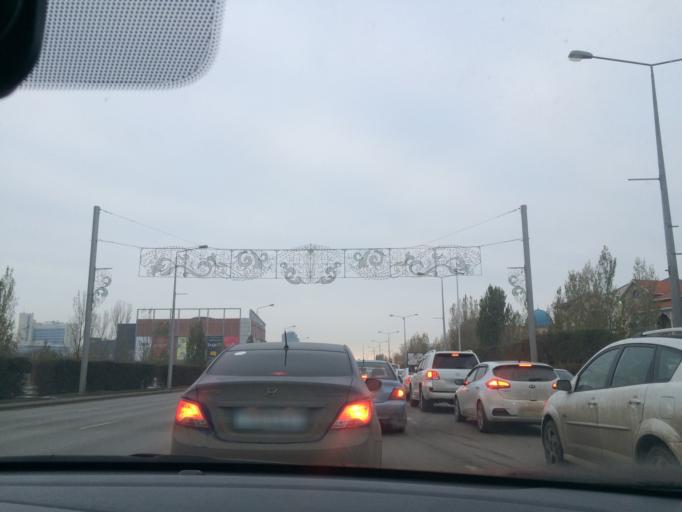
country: KZ
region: Astana Qalasy
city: Astana
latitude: 51.1416
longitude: 71.4103
